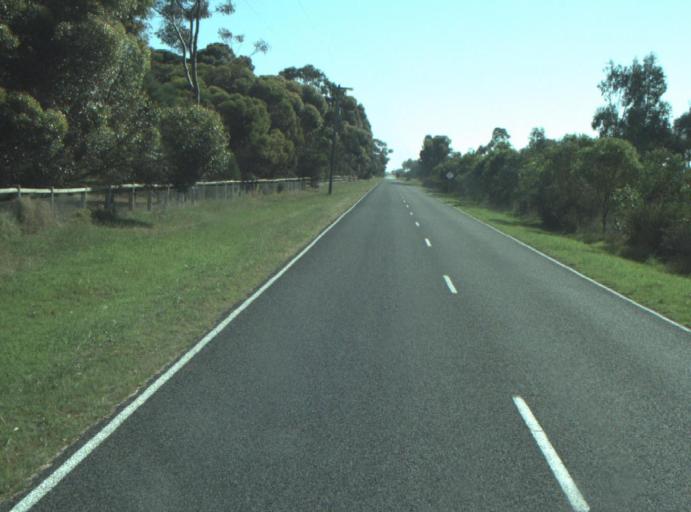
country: AU
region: Victoria
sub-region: Greater Geelong
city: Lara
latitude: -38.0022
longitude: 144.4394
